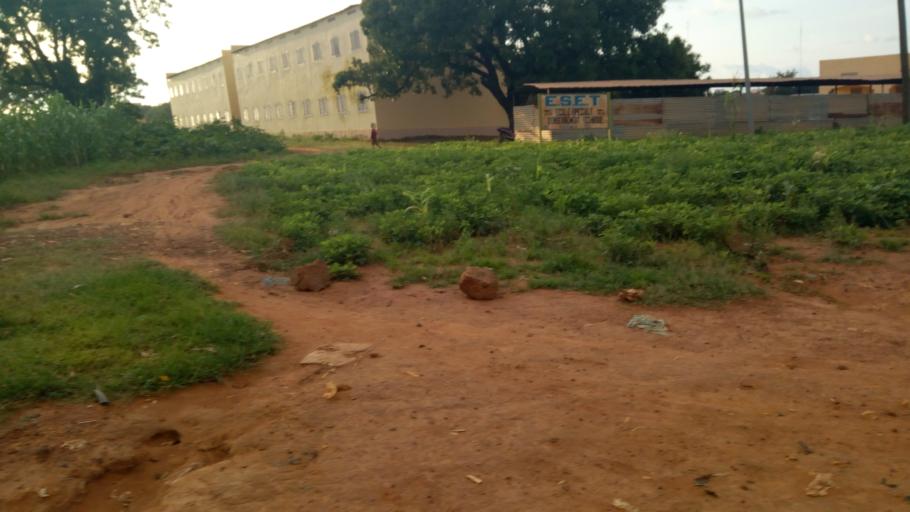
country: ML
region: Sikasso
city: Koutiala
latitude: 12.3761
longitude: -5.4738
